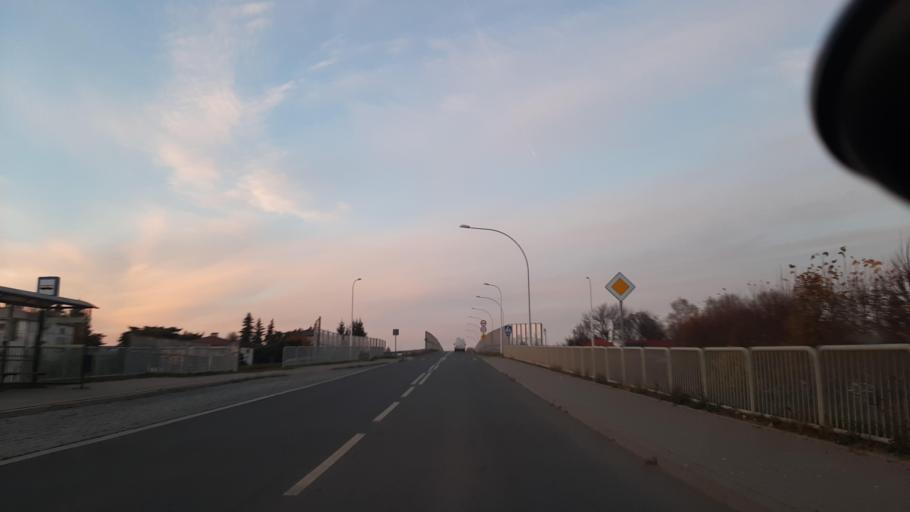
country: PL
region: Lublin Voivodeship
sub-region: Powiat lubelski
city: Jastkow
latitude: 51.2988
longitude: 22.4932
